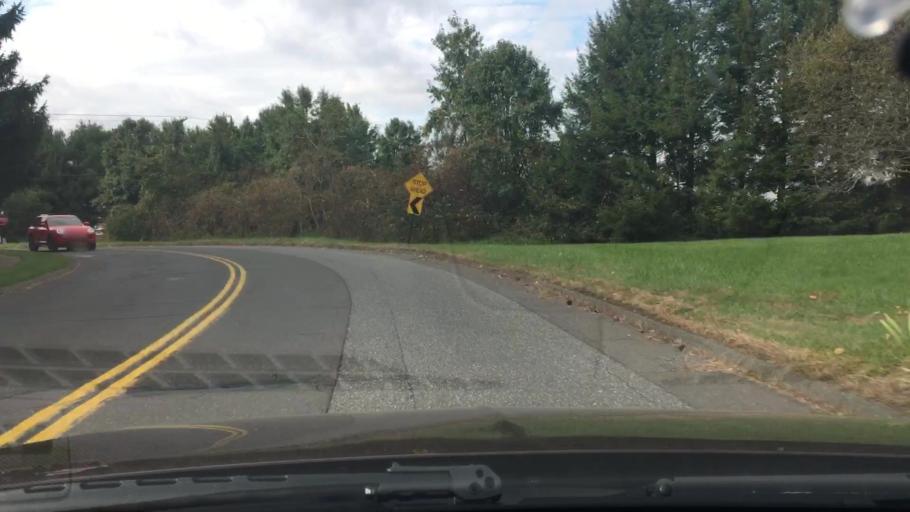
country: US
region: Connecticut
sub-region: Hartford County
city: Hazardville
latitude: 42.0081
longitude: -72.5116
